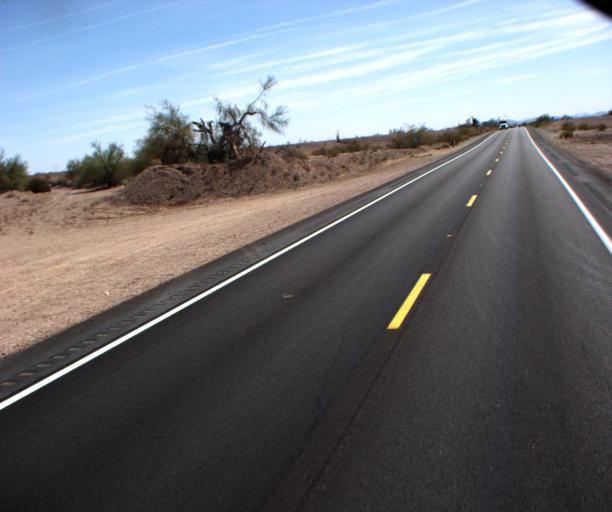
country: US
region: Arizona
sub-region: Yuma County
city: Wellton
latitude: 33.0490
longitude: -114.2910
